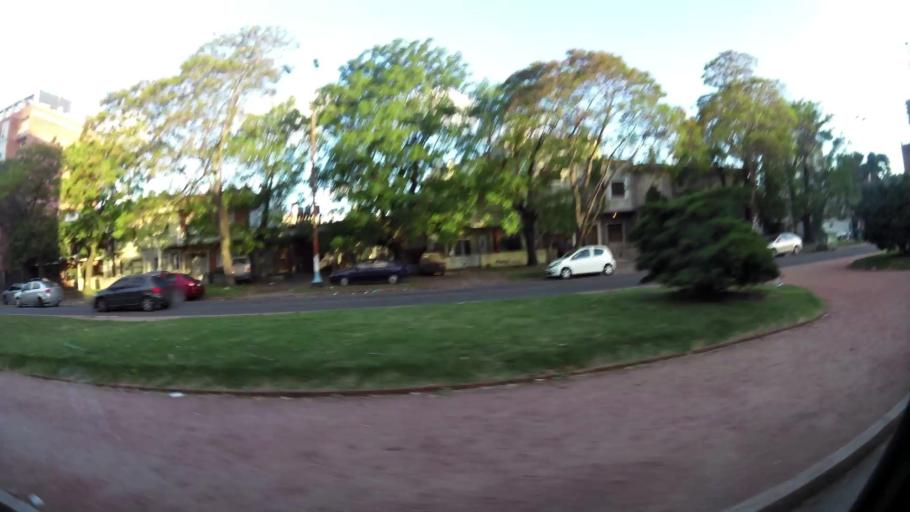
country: UY
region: Montevideo
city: Montevideo
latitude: -34.8896
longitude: -56.1547
